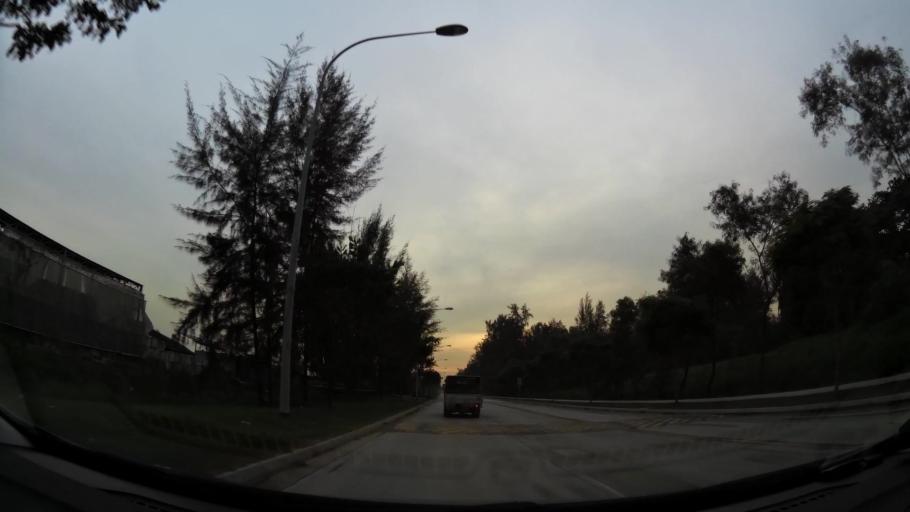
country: SG
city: Singapore
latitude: 1.2914
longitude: 103.8828
